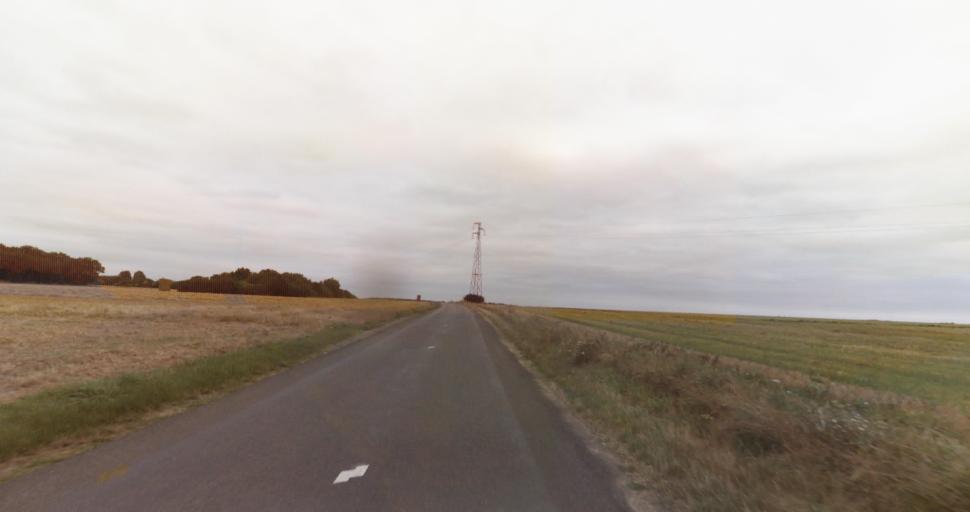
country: FR
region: Centre
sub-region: Departement d'Eure-et-Loir
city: Vert-en-Drouais
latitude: 48.7877
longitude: 1.2889
